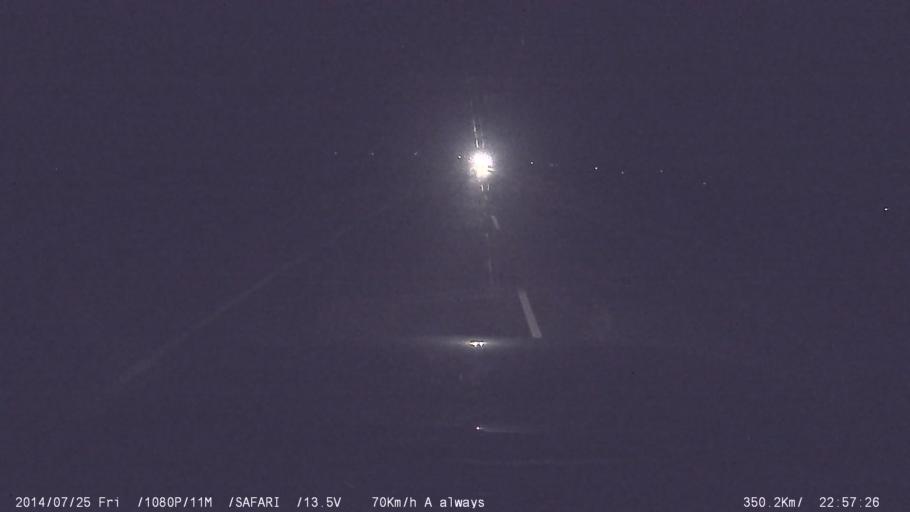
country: IN
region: Tamil Nadu
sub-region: Coimbatore
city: Singanallur
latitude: 10.9739
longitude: 77.0403
